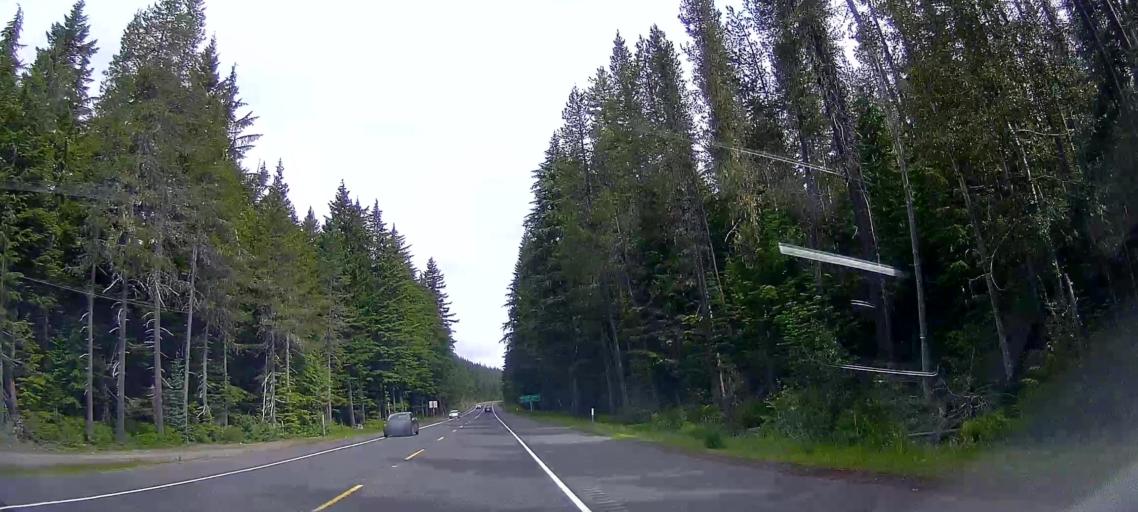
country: US
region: Oregon
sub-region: Clackamas County
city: Mount Hood Village
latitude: 45.2627
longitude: -121.7148
